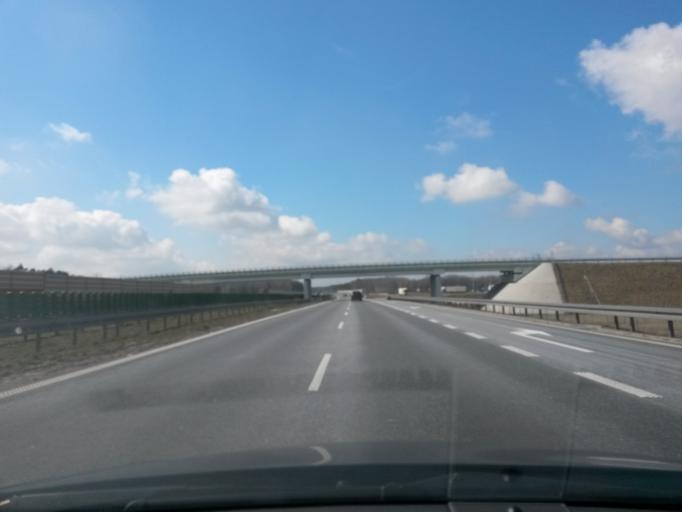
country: PL
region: Lodz Voivodeship
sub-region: Powiat skierniewicki
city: Bolimow
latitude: 52.0753
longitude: 20.2418
